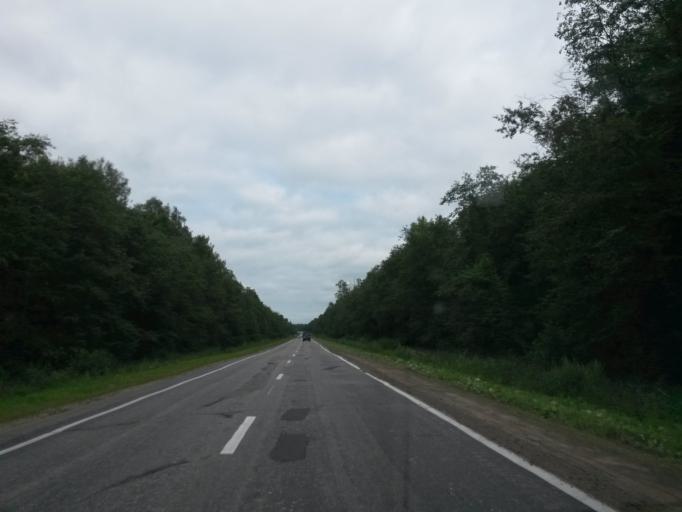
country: RU
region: Jaroslavl
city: Gavrilov-Yam
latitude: 57.4324
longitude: 39.9182
